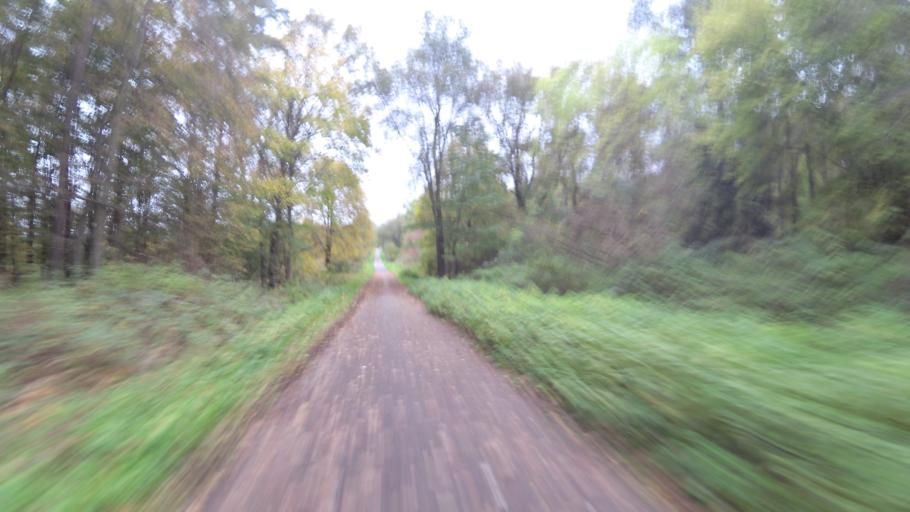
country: DE
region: Saarland
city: Homburg
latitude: 49.2972
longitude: 7.3194
